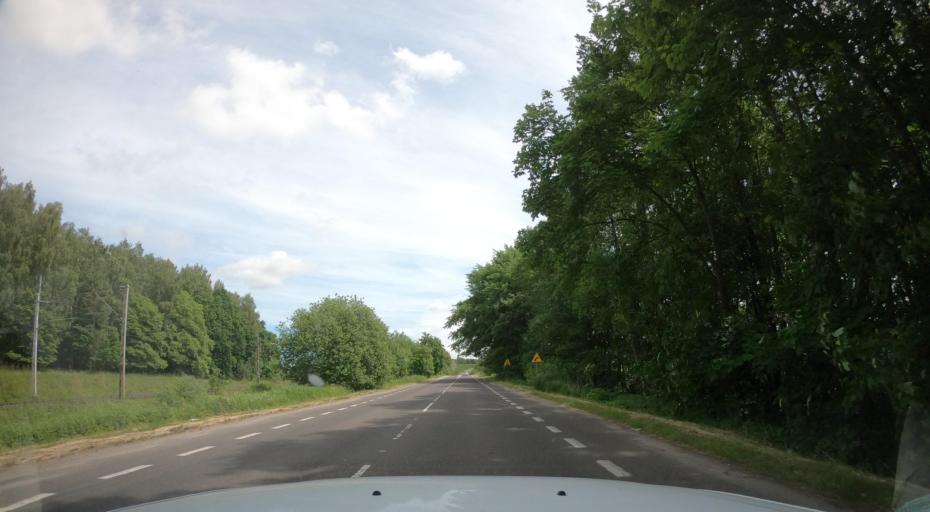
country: PL
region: West Pomeranian Voivodeship
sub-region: Powiat goleniowski
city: Przybiernow
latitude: 53.8450
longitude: 14.7394
